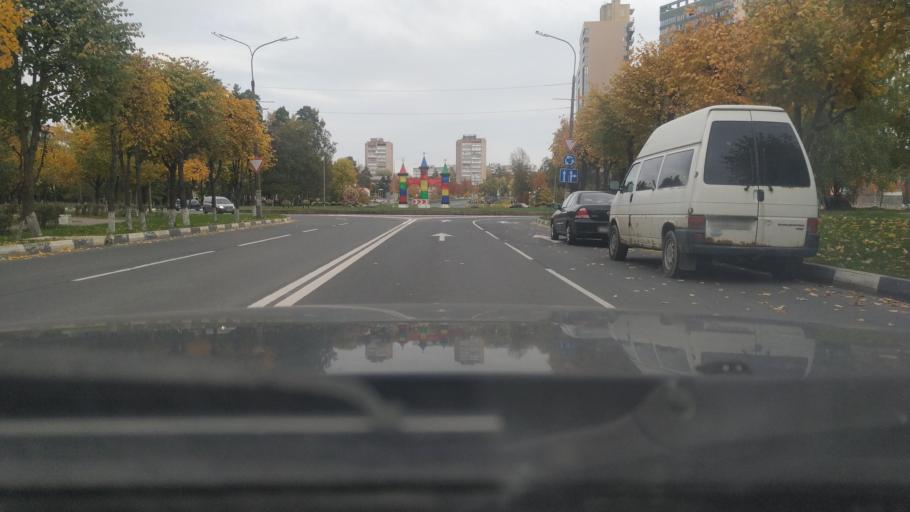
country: RU
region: Leningrad
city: Sosnovyy Bor
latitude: 59.9035
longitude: 29.0913
